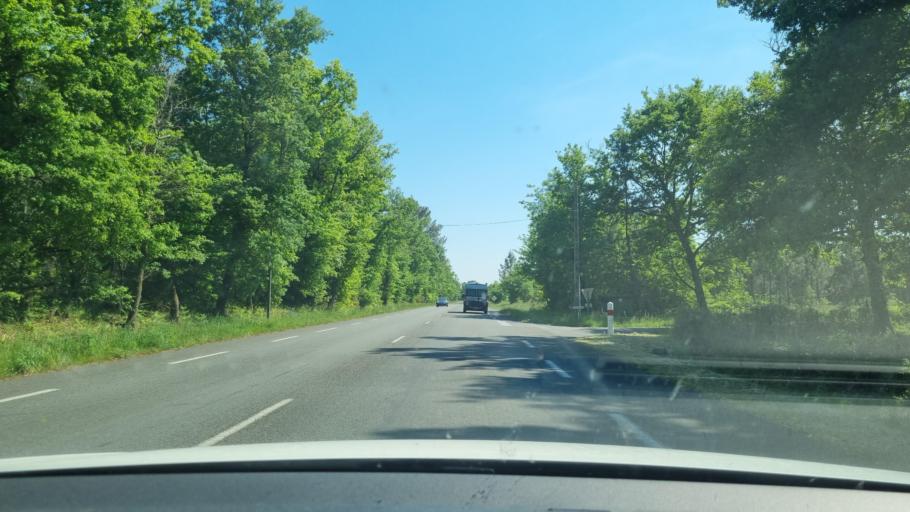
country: FR
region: Aquitaine
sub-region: Departement de la Gironde
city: Prechac
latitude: 44.2371
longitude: -0.2608
